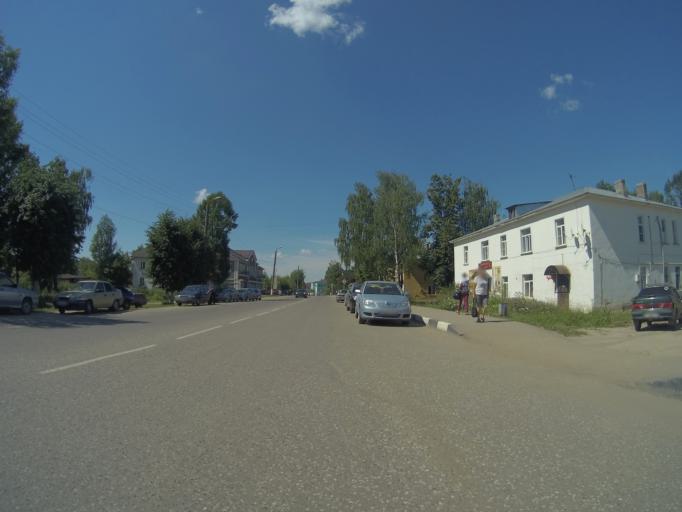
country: RU
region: Ivanovo
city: Privolzhsk
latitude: 57.3800
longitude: 41.2927
